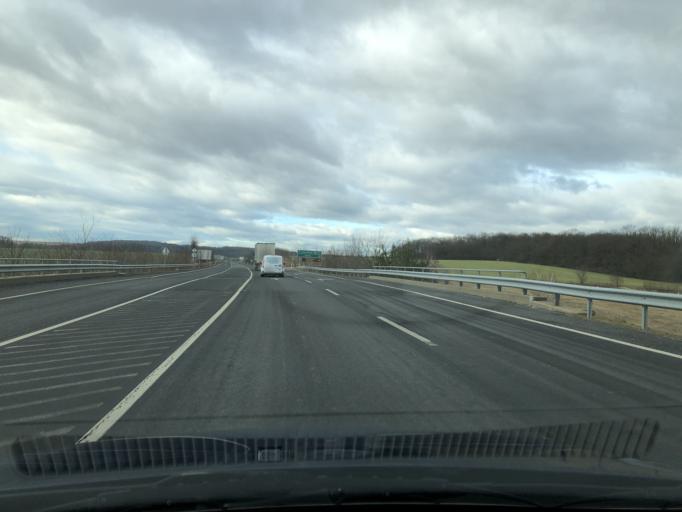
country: AT
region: Burgenland
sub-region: Politischer Bezirk Oberwart
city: Schachendorf
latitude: 47.2476
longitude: 16.4986
